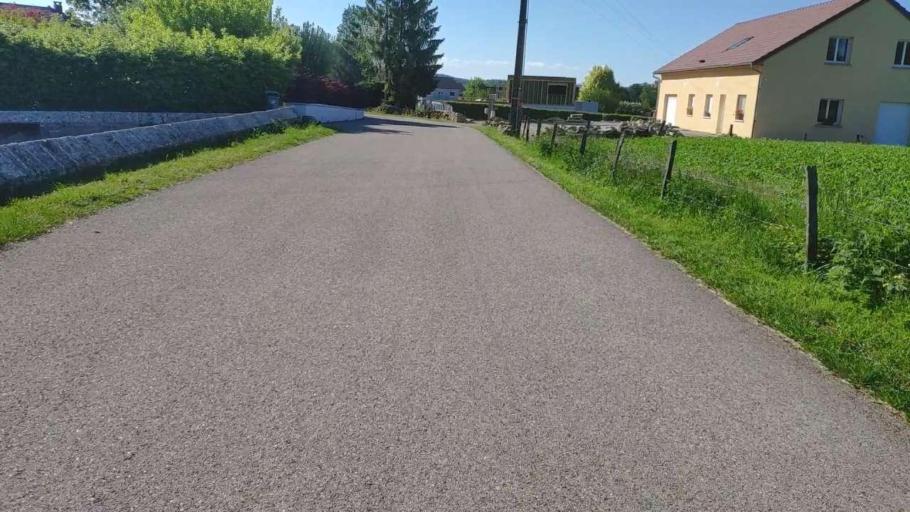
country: FR
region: Franche-Comte
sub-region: Departement du Jura
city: Perrigny
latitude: 46.6856
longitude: 5.6552
